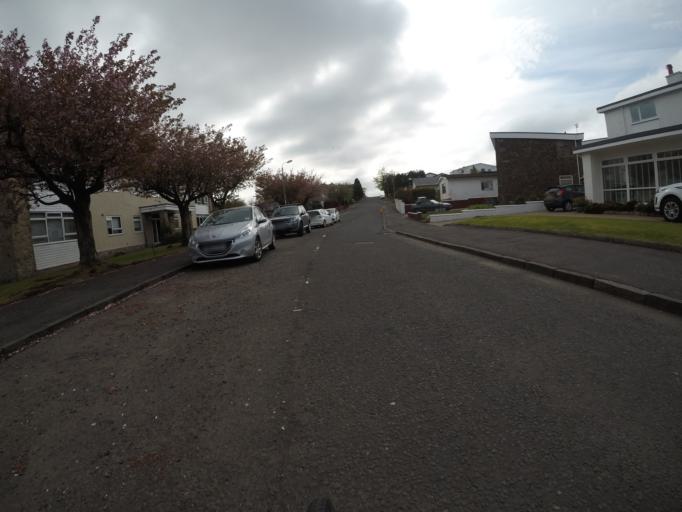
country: GB
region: Scotland
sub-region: East Renfrewshire
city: Busby
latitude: 55.7783
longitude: -4.3028
